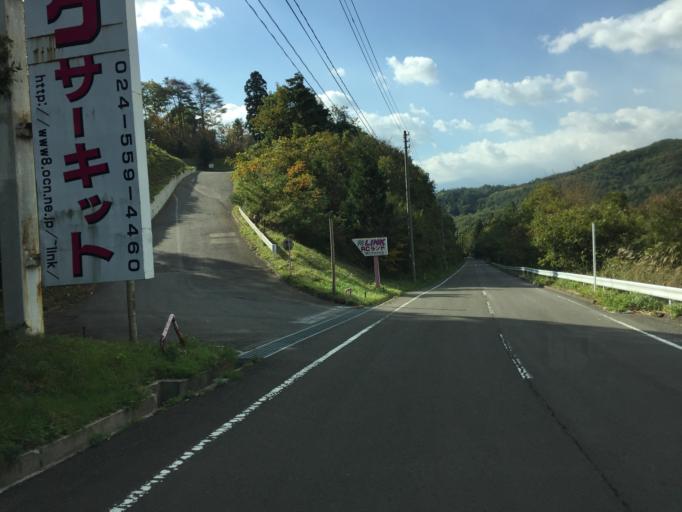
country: JP
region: Fukushima
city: Fukushima-shi
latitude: 37.8034
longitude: 140.3891
